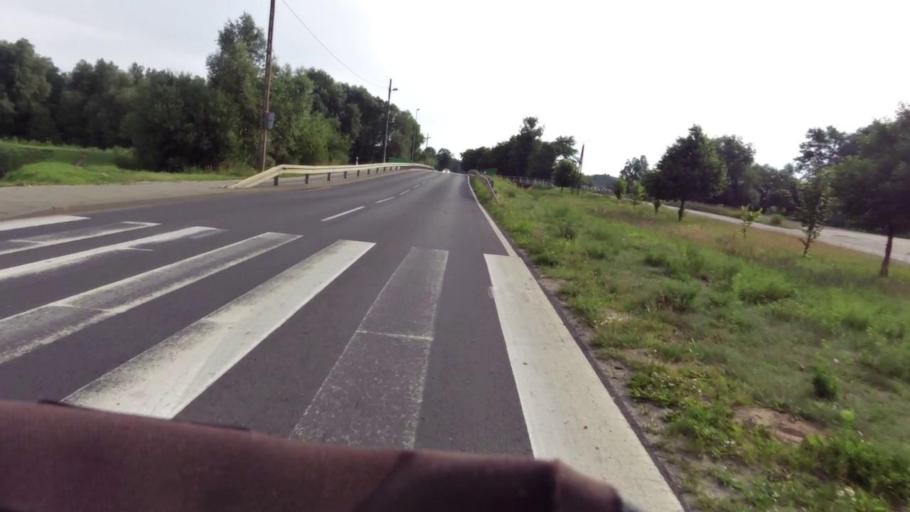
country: PL
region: West Pomeranian Voivodeship
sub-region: Powiat kamienski
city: Kamien Pomorski
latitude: 53.9720
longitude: 14.7856
